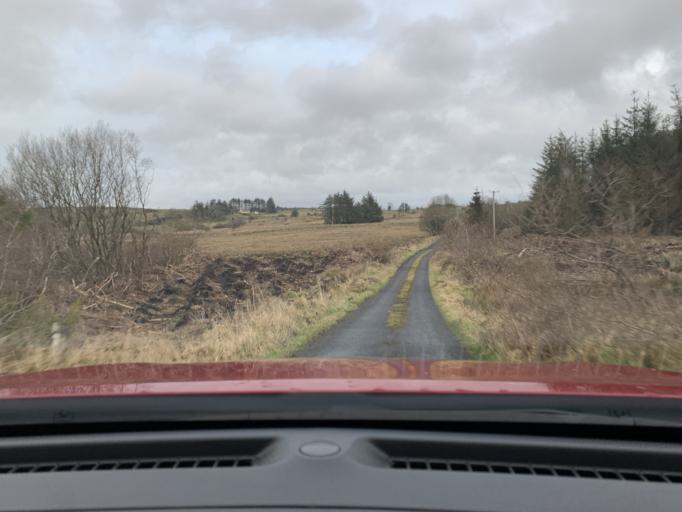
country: IE
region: Connaught
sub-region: Roscommon
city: Boyle
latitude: 53.9896
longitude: -8.4134
